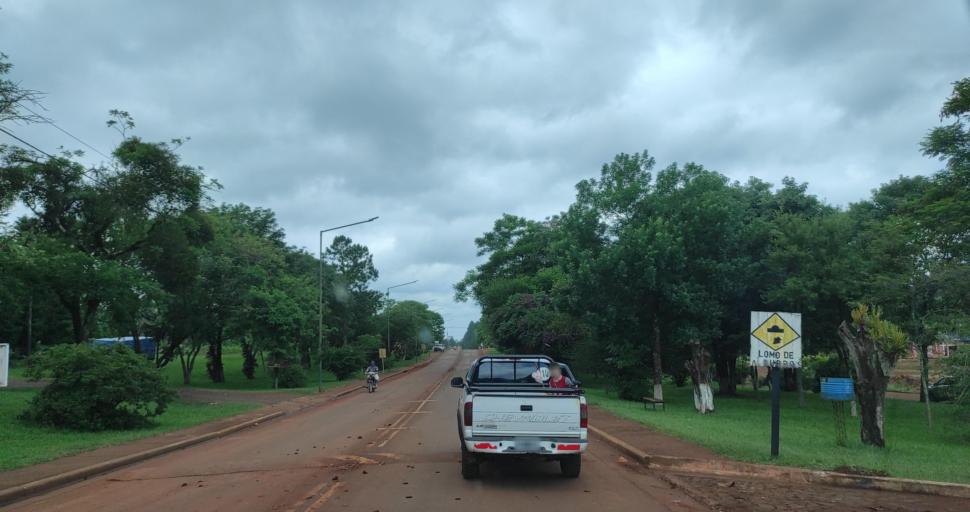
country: AR
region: Misiones
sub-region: Departamento de Veinticinco de Mayo
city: Veinticinco de Mayo
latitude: -27.3844
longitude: -54.7454
